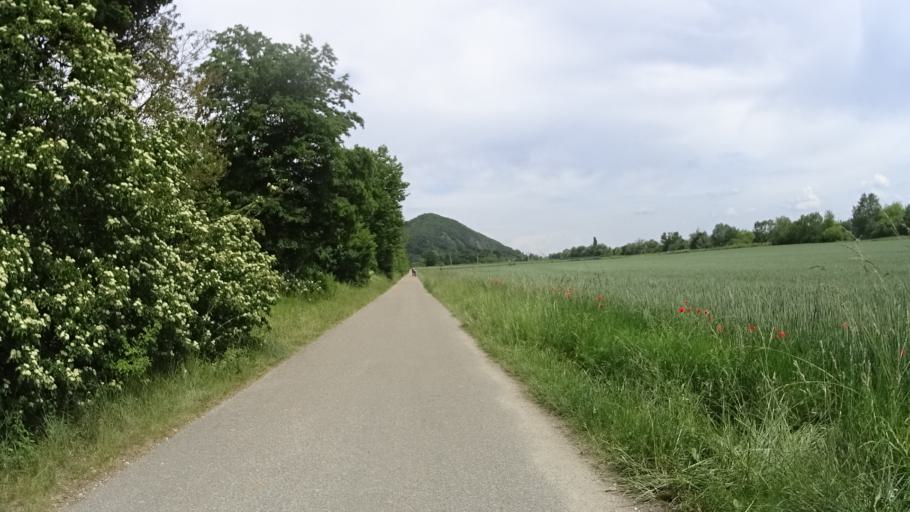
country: DE
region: Bavaria
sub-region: Upper Palatinate
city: Donaustauf
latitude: 49.0290
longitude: 12.2256
